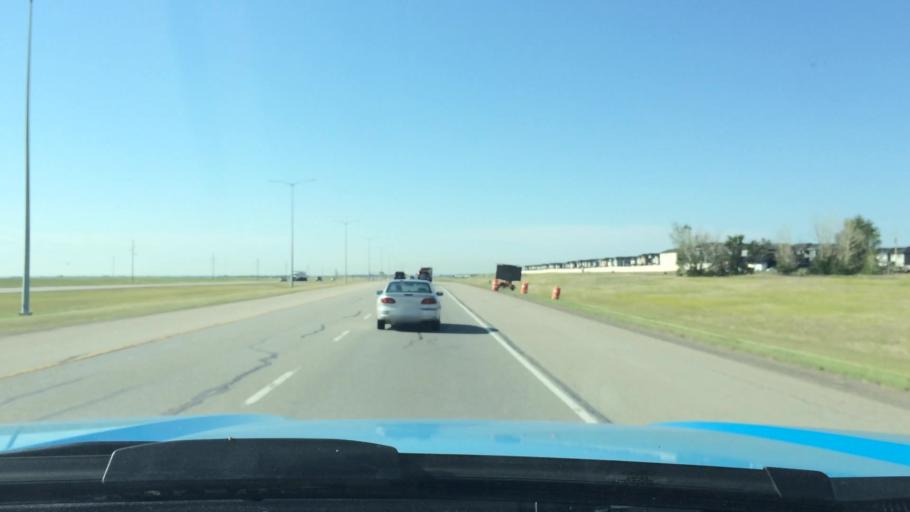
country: CA
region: Alberta
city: Chestermere
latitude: 51.1274
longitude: -113.9216
